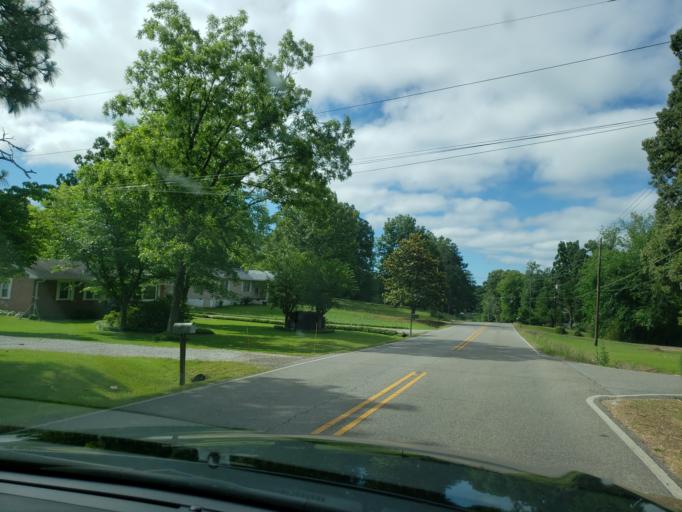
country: US
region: Alabama
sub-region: Calhoun County
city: Saks
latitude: 33.7183
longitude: -85.8452
